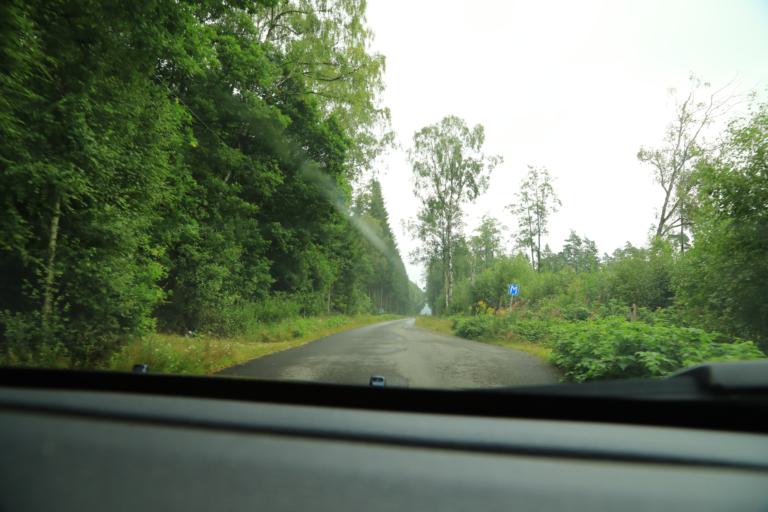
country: SE
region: Halland
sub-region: Falkenbergs Kommun
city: Falkenberg
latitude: 57.1053
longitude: 12.6606
